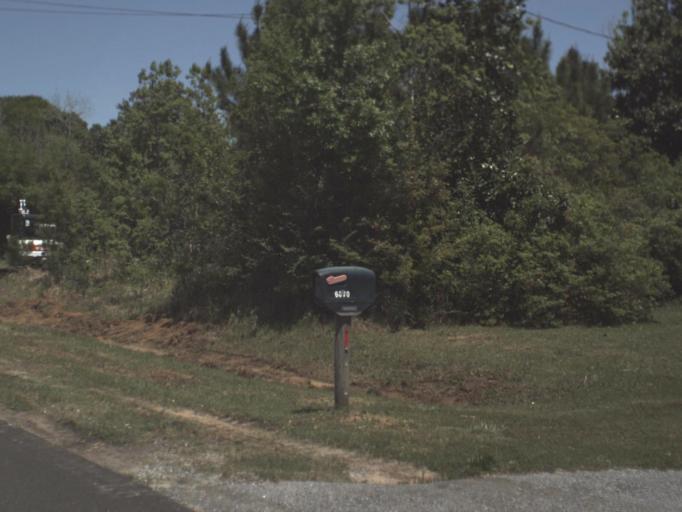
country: US
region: Florida
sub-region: Escambia County
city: Bellview
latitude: 30.4646
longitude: -87.3241
